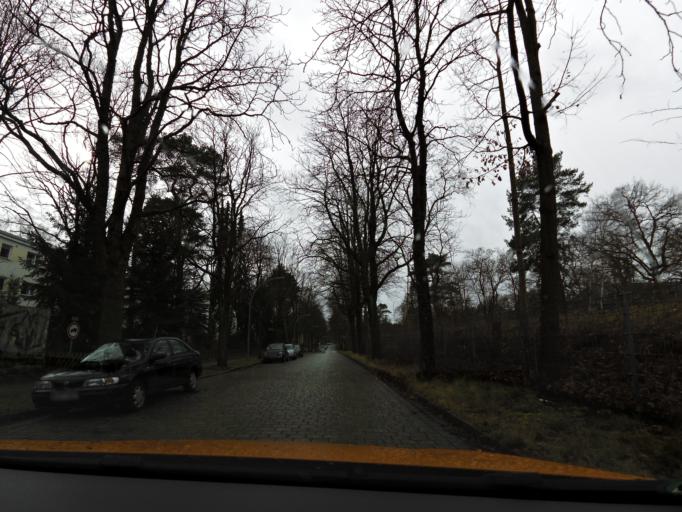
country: DE
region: Berlin
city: Nikolassee
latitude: 52.4380
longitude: 13.2074
